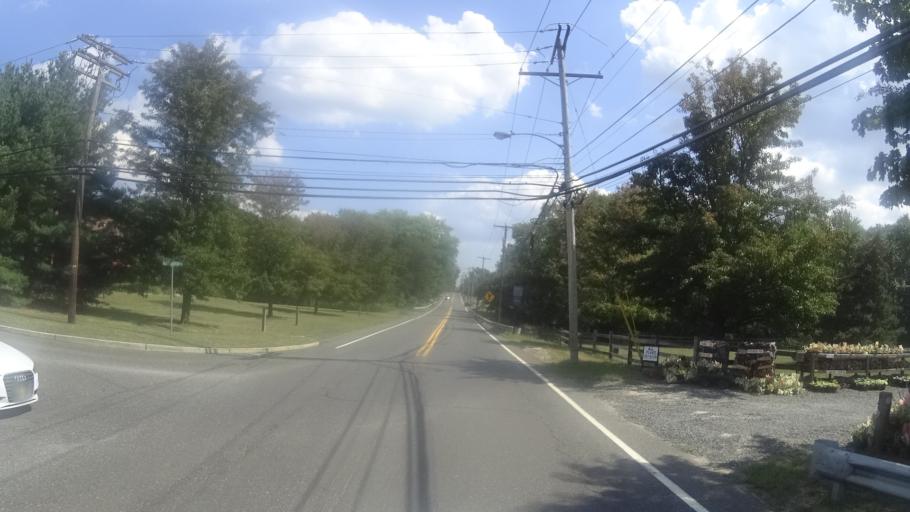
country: US
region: New Jersey
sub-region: Monmouth County
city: Ramtown
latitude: 40.1474
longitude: -74.1050
